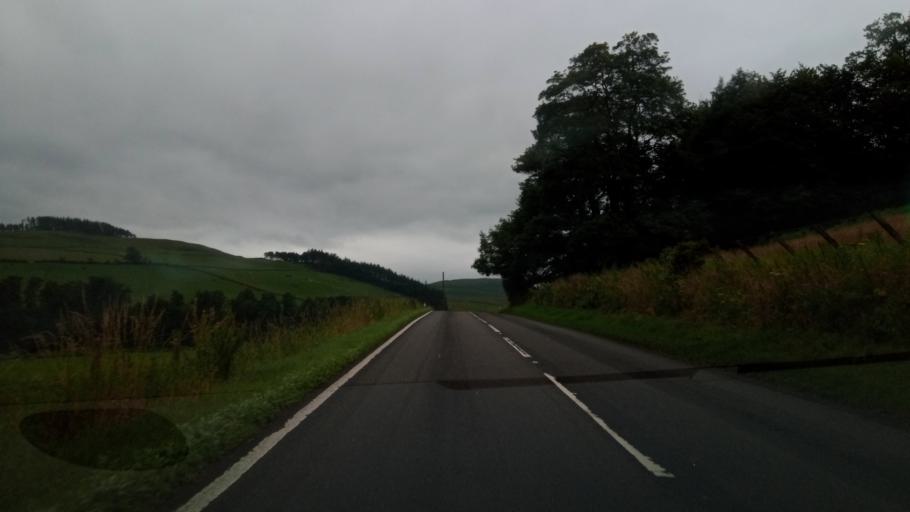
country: GB
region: Scotland
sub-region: The Scottish Borders
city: Hawick
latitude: 55.3685
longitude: -2.8803
